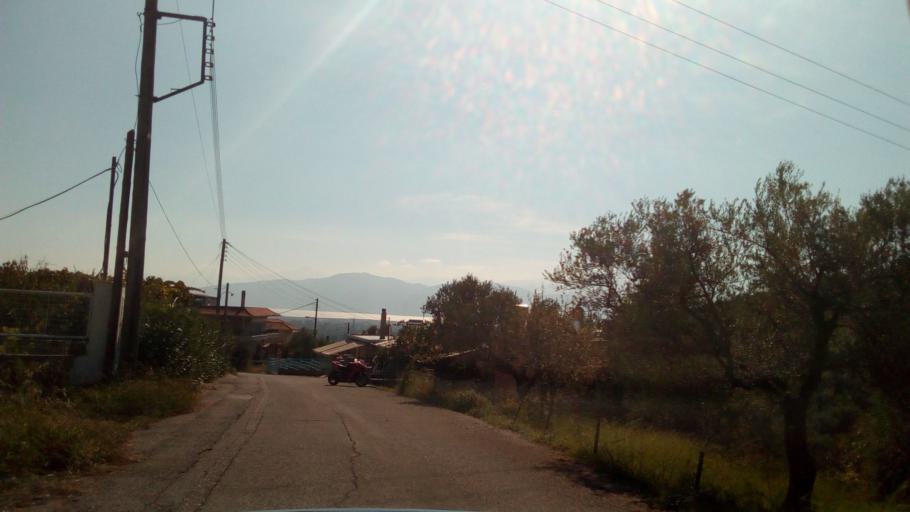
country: GR
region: West Greece
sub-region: Nomos Aitolias kai Akarnanias
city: Nafpaktos
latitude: 38.4191
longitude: 21.8707
